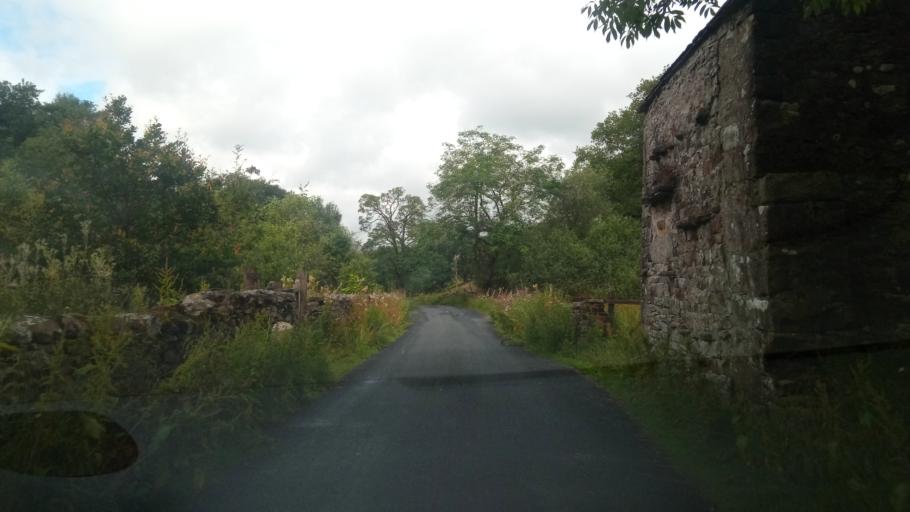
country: GB
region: England
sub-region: North Yorkshire
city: Ingleton
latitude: 54.2585
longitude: -2.3467
